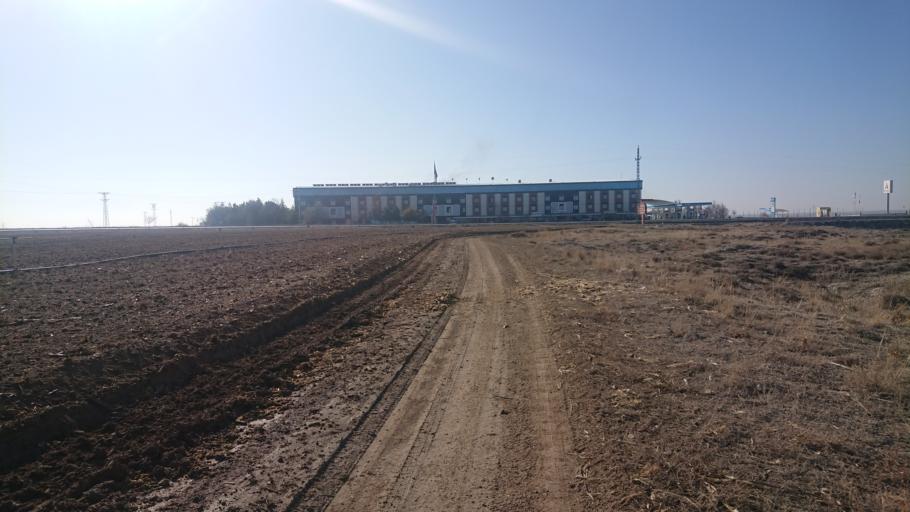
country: TR
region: Aksaray
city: Sultanhani
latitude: 38.2536
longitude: 33.5081
